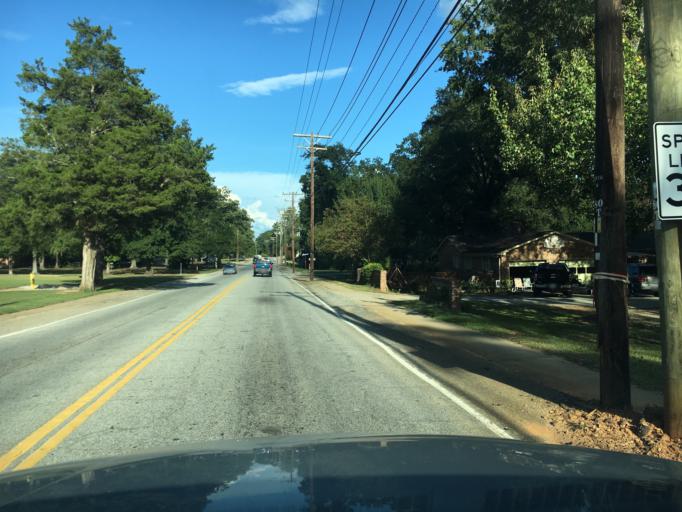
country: US
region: South Carolina
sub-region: Greenville County
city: Simpsonville
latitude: 34.7390
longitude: -82.2499
